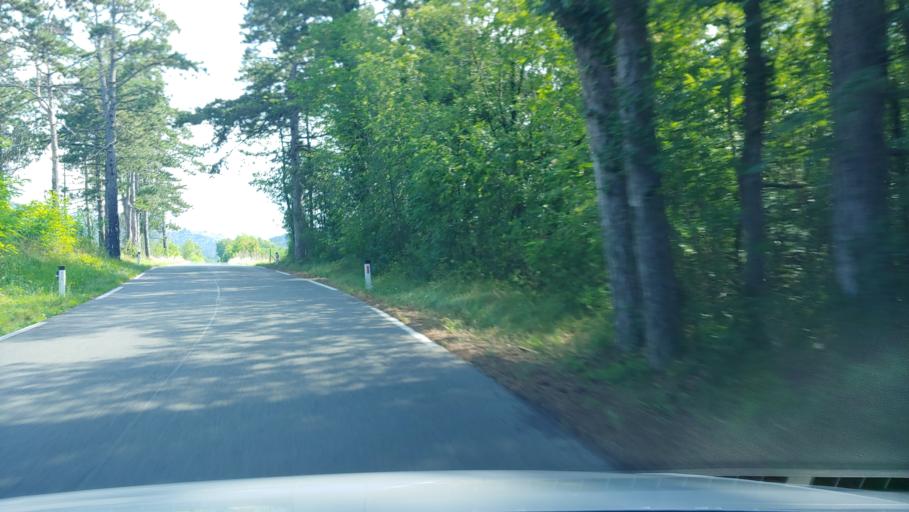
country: SI
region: Komen
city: Komen
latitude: 45.8286
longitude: 13.7610
